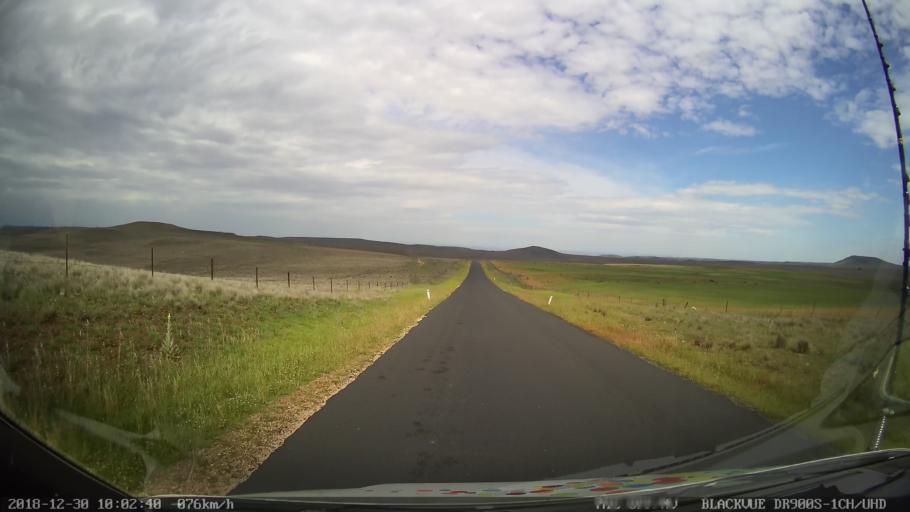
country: AU
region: New South Wales
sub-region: Cooma-Monaro
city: Cooma
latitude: -36.5156
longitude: 149.1683
